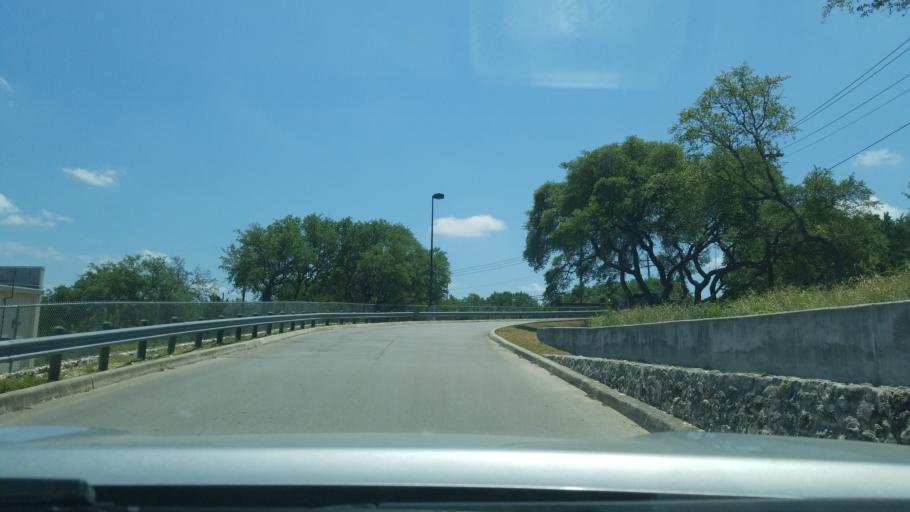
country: US
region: Texas
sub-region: Comal County
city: Bulverde
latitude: 29.7973
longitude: -98.4283
